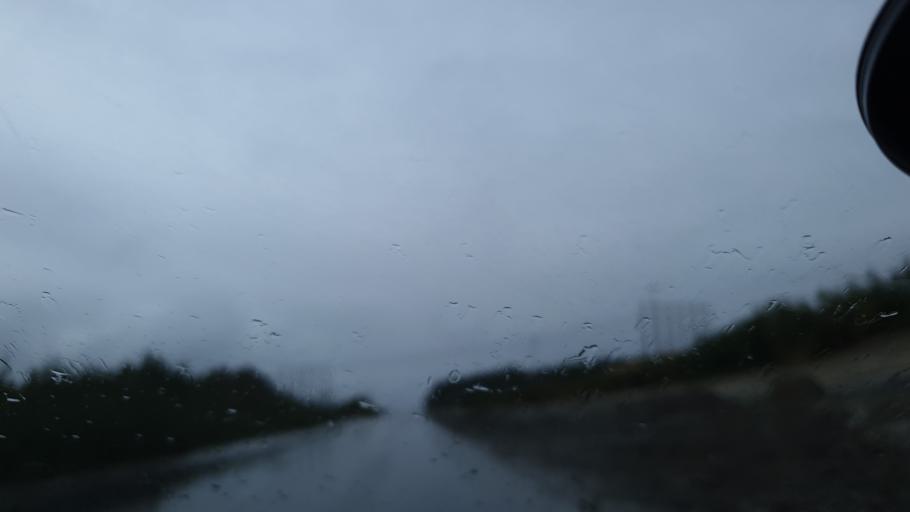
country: SE
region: Vaesterbotten
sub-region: Skelleftea Kommun
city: Soedra Bergsbyn
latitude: 64.7435
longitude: 21.0631
